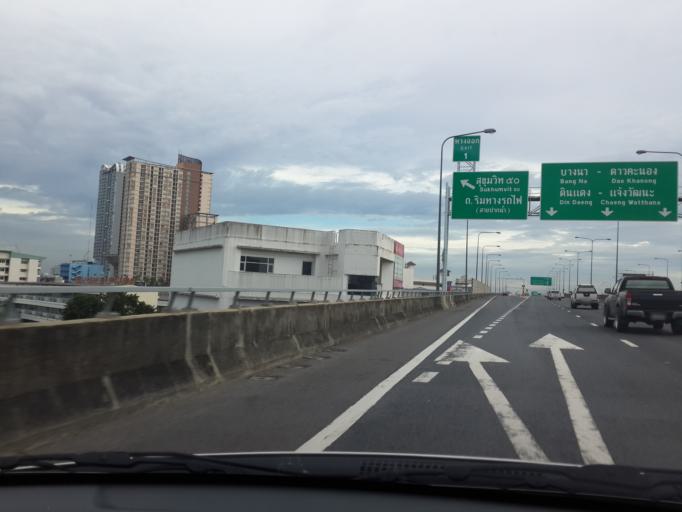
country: TH
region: Bangkok
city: Phra Khanong
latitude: 13.7123
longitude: 100.5990
